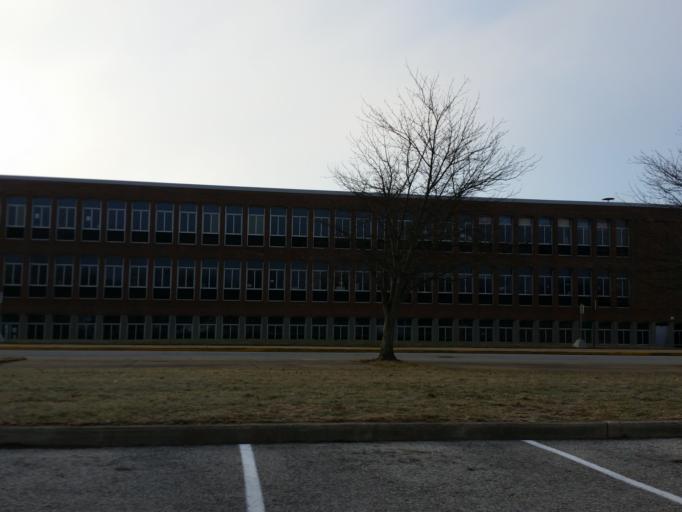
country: US
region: Indiana
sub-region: Bartholomew County
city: Columbus
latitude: 39.2287
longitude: -85.9091
